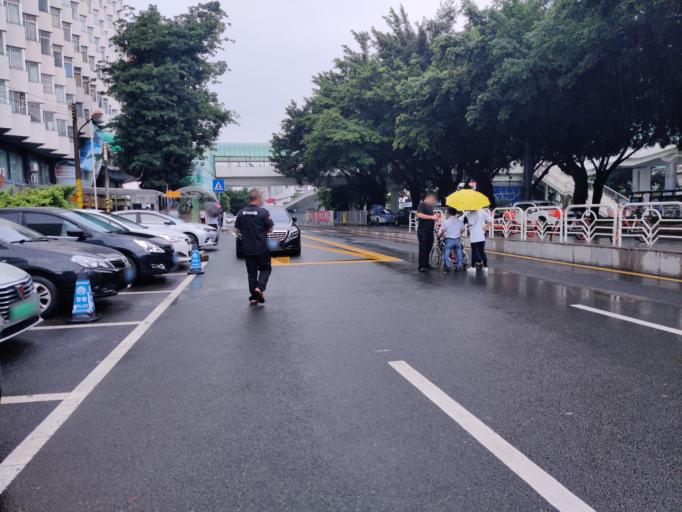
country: CN
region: Guangdong
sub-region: Shenzhen
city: Shenzhen
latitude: 22.5308
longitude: 114.1115
